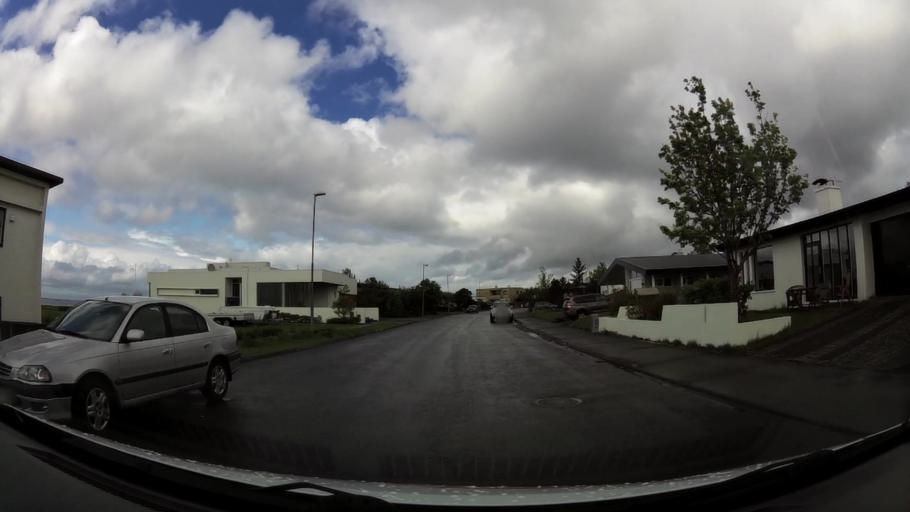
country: IS
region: Capital Region
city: Kopavogur
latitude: 64.1283
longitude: -21.9555
